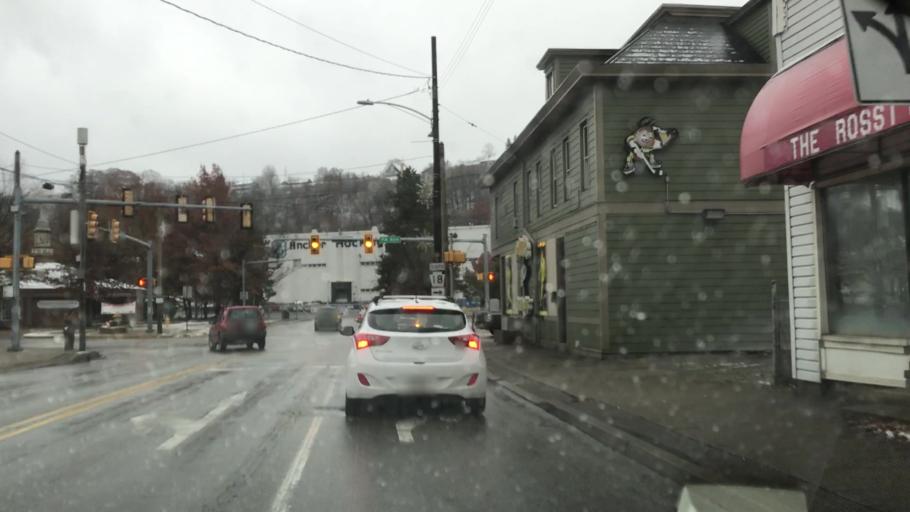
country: US
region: Pennsylvania
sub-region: Beaver County
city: Monaca
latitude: 40.6919
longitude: -80.2809
